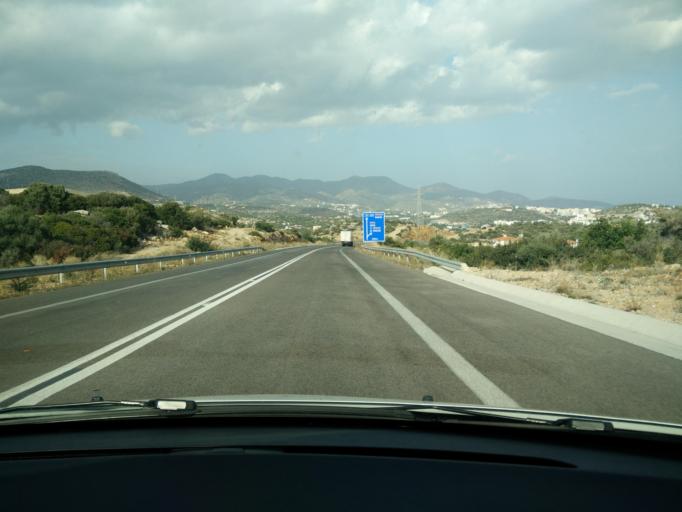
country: GR
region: Crete
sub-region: Nomos Lasithiou
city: Agios Nikolaos
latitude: 35.1761
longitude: 25.7009
